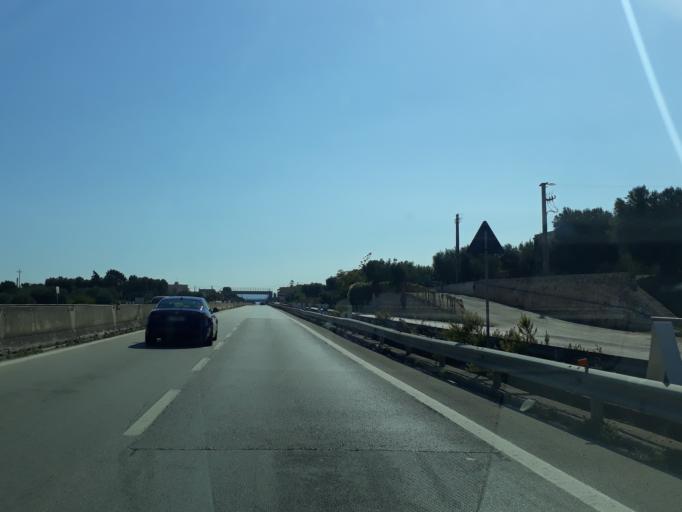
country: IT
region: Apulia
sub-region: Provincia di Brindisi
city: Fasano
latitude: 40.8878
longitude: 17.3343
